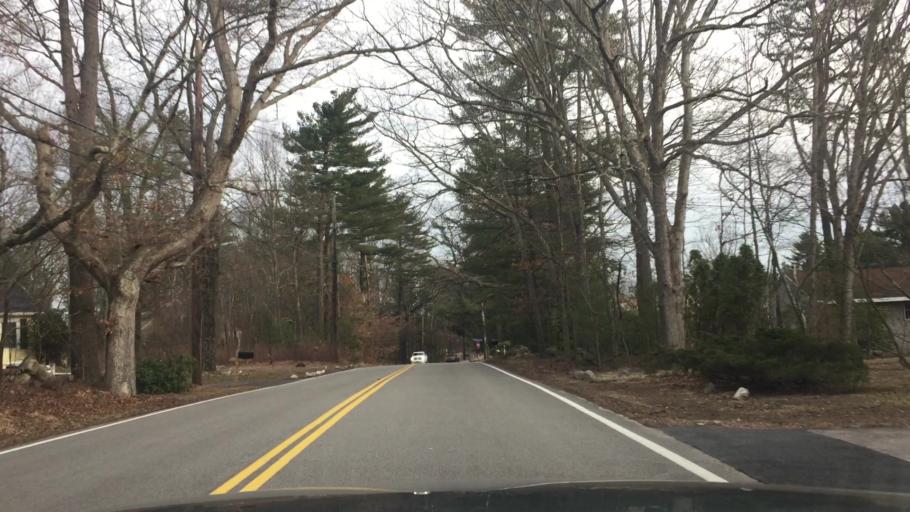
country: US
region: Massachusetts
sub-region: Norfolk County
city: Medway
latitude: 42.1415
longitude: -71.4536
